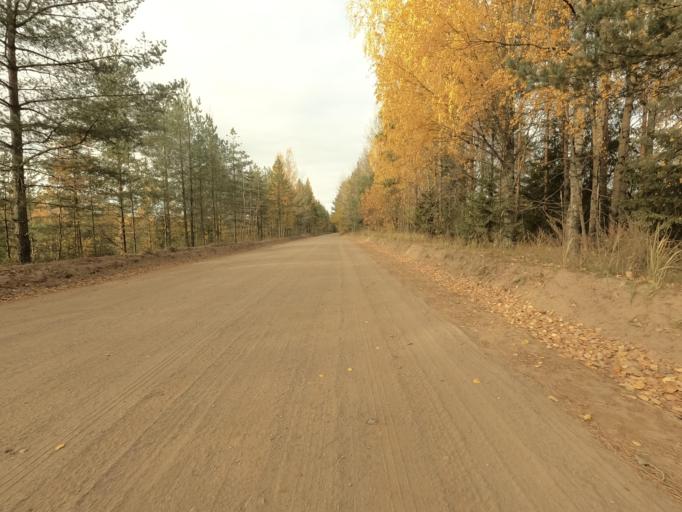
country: RU
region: Leningrad
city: Priladozhskiy
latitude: 59.6768
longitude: 31.3656
